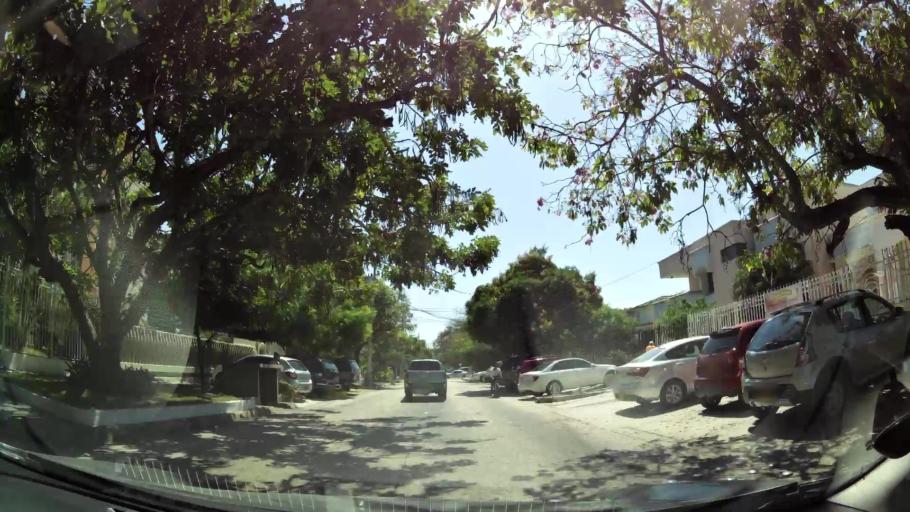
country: CO
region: Atlantico
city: Barranquilla
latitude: 11.0054
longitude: -74.8002
